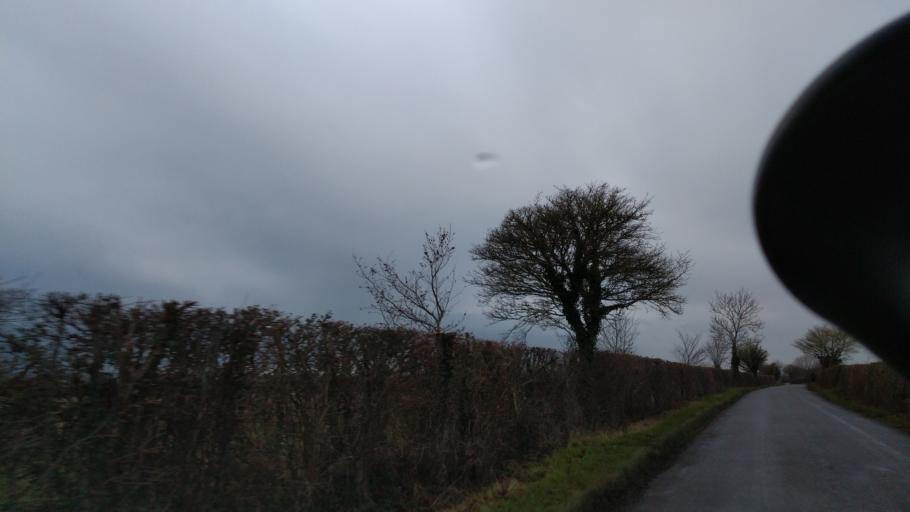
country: GB
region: England
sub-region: Borough of Swindon
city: Highworth
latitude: 51.6086
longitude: -1.7185
